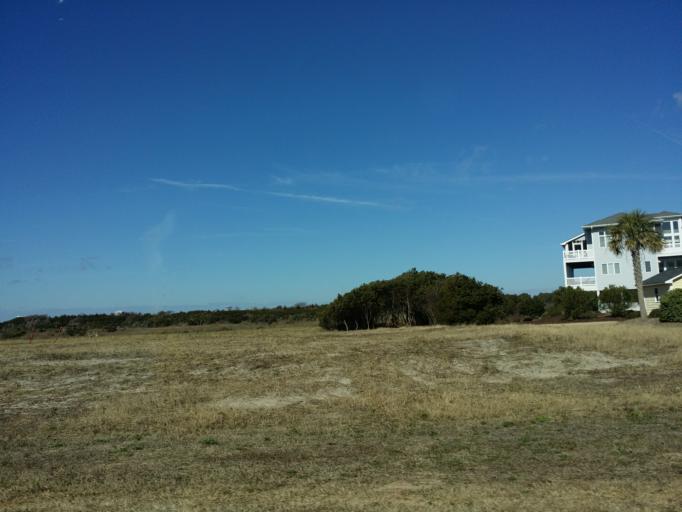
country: US
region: North Carolina
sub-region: Onslow County
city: Holly Ridge
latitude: 34.4739
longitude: -77.4611
